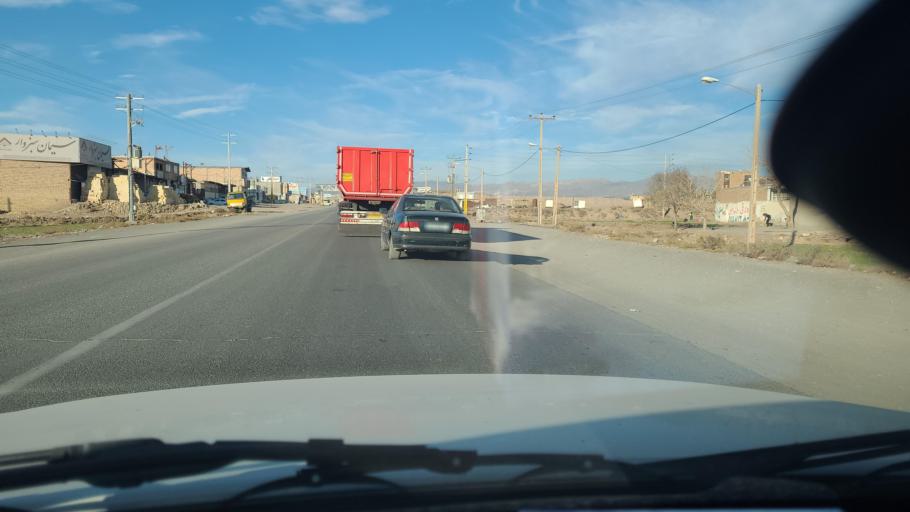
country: IR
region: Razavi Khorasan
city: Sabzevar
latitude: 36.2189
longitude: 57.6513
